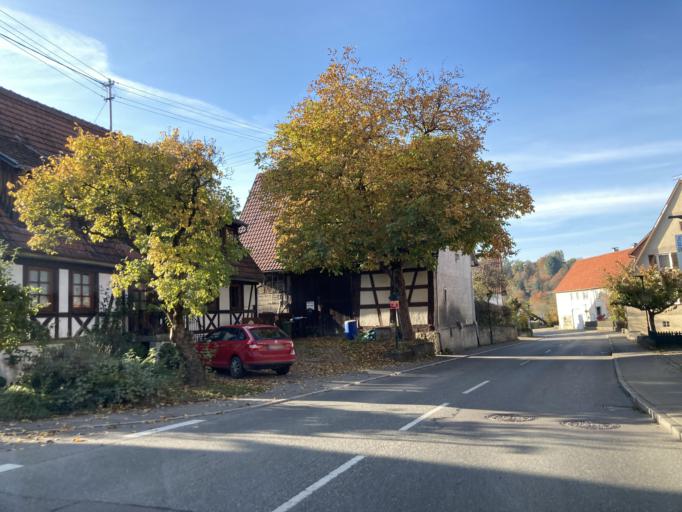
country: DE
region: Baden-Wuerttemberg
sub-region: Tuebingen Region
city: Nehren
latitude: 48.4145
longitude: 9.1046
